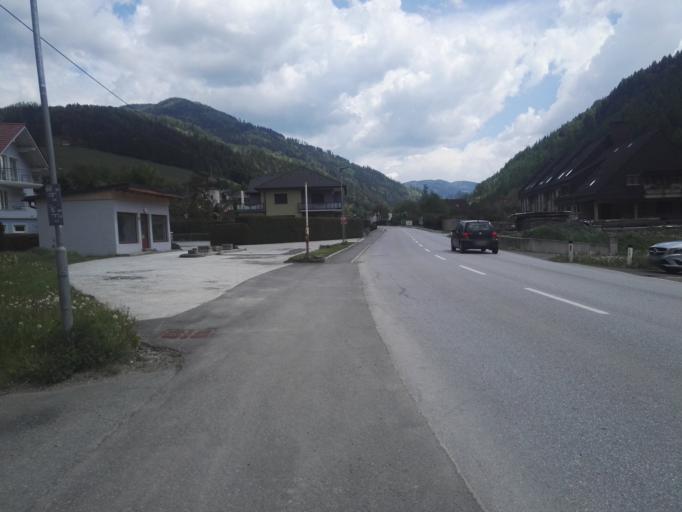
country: AT
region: Styria
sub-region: Politischer Bezirk Bruck-Muerzzuschlag
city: Allerheiligen im Muerztal
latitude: 47.3906
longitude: 15.4258
